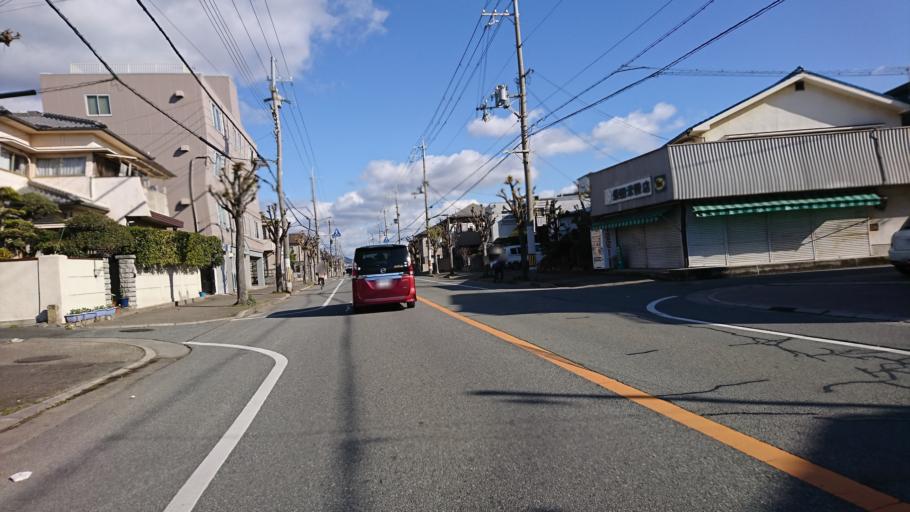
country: JP
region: Hyogo
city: Kakogawacho-honmachi
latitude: 34.7614
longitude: 134.7943
